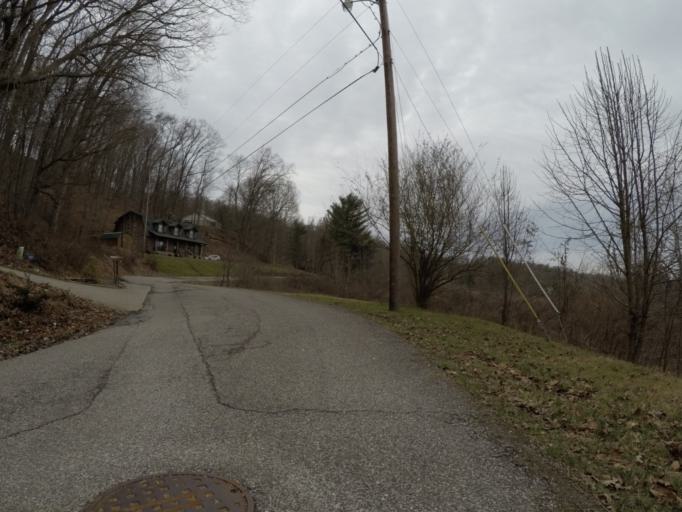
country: US
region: Ohio
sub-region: Lawrence County
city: Burlington
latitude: 38.3828
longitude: -82.5057
